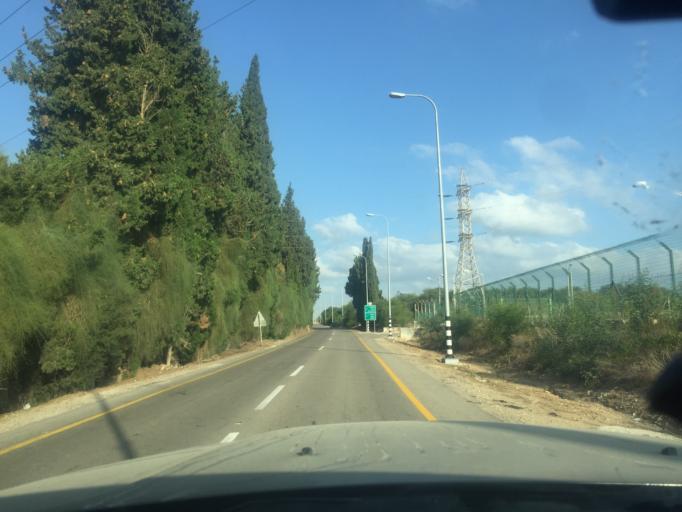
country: IL
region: Southern District
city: Ashqelon
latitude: 31.6028
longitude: 34.5704
